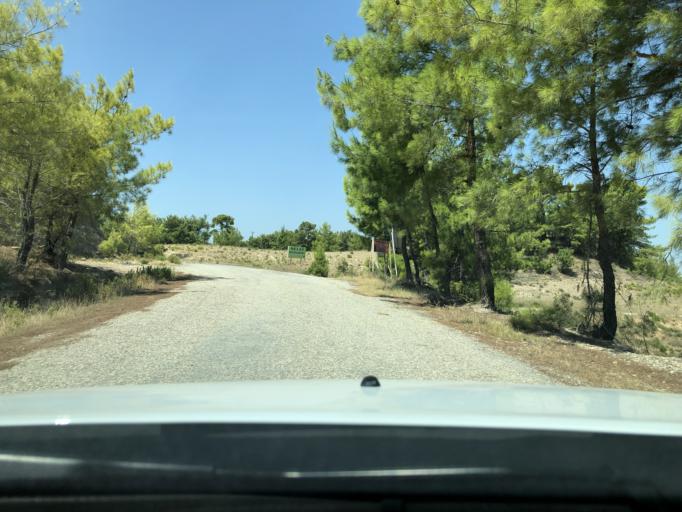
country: TR
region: Antalya
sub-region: Manavgat
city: Manavgat
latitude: 36.8371
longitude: 31.5348
